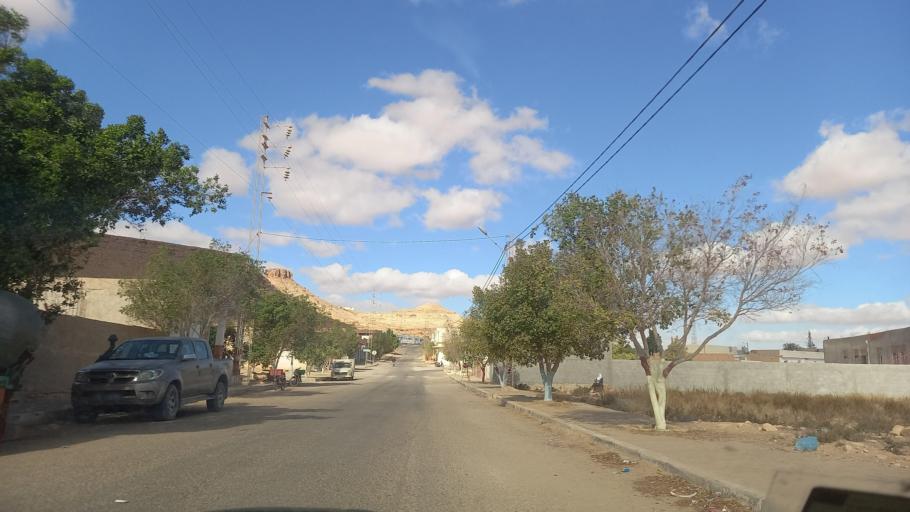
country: TN
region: Tataouine
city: Tataouine
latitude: 32.9812
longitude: 10.2665
